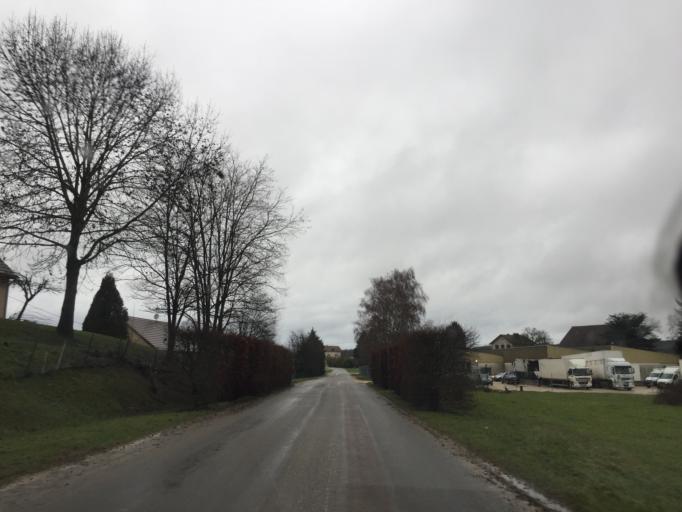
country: FR
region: Franche-Comte
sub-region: Departement du Jura
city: Orchamps
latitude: 47.1945
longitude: 5.6493
